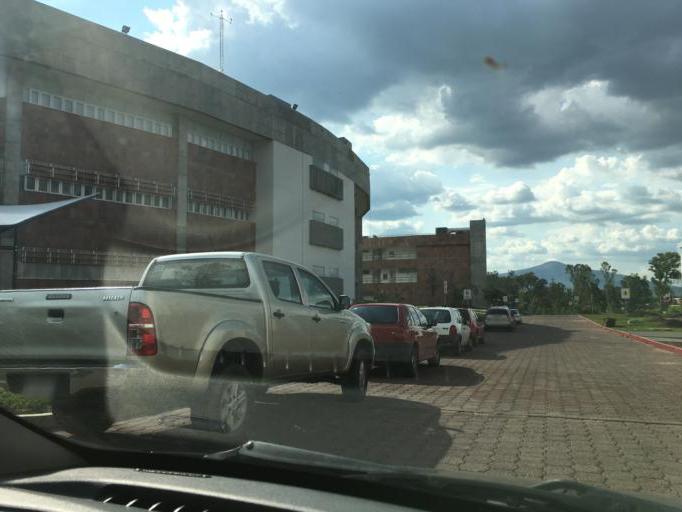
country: MX
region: Michoacan
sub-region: Morelia
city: Morelos
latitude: 19.6490
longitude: -101.2217
